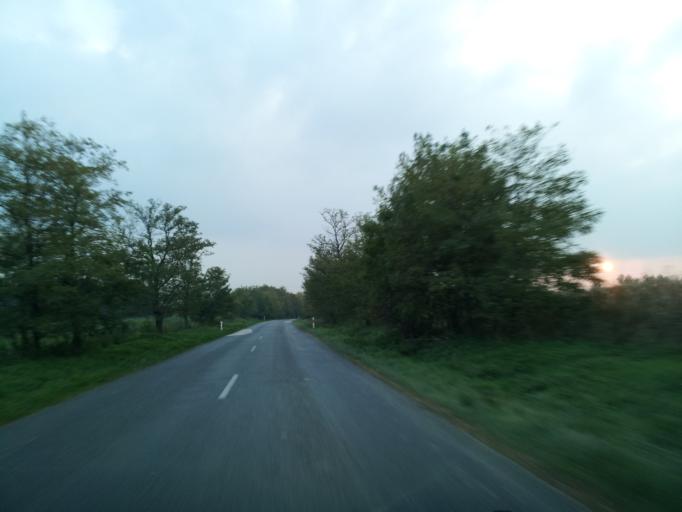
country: HU
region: Gyor-Moson-Sopron
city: Bakonyszentlaszlo
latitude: 47.4501
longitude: 17.8202
